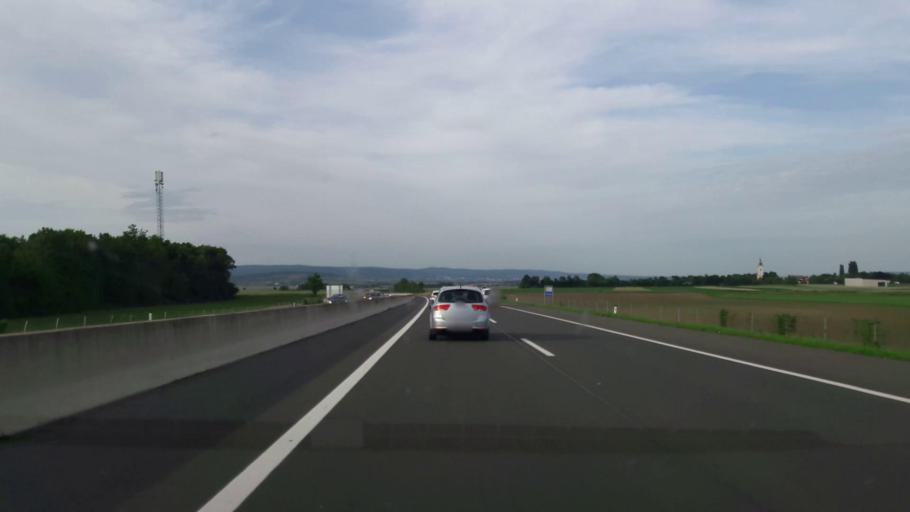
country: AT
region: Burgenland
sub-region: Politischer Bezirk Mattersburg
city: Krensdorf
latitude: 47.7680
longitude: 16.4244
